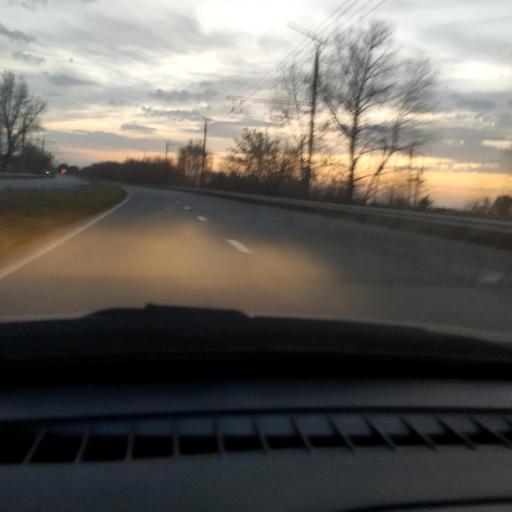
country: RU
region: Samara
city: Zhigulevsk
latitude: 53.5480
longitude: 49.5906
